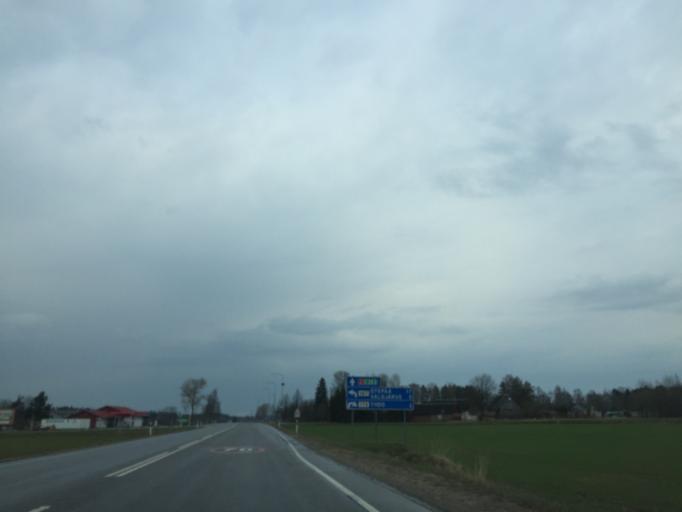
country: EE
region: Tartu
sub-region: UElenurme vald
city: Ulenurme
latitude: 58.0643
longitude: 26.7306
